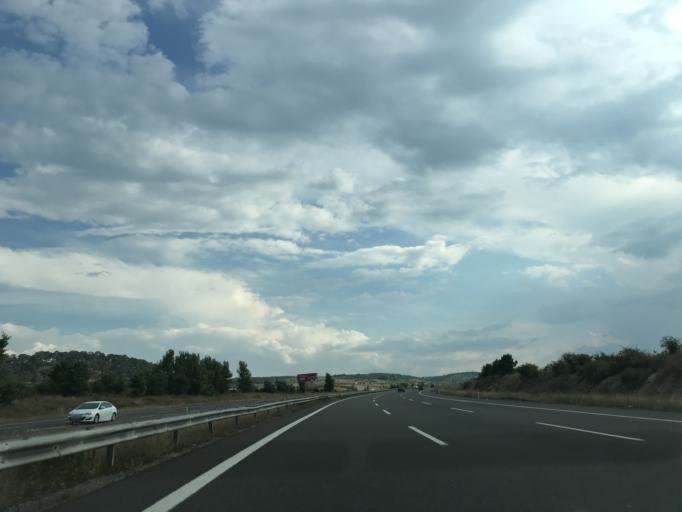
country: TR
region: Bolu
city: Gerede
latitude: 40.6648
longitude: 32.2397
